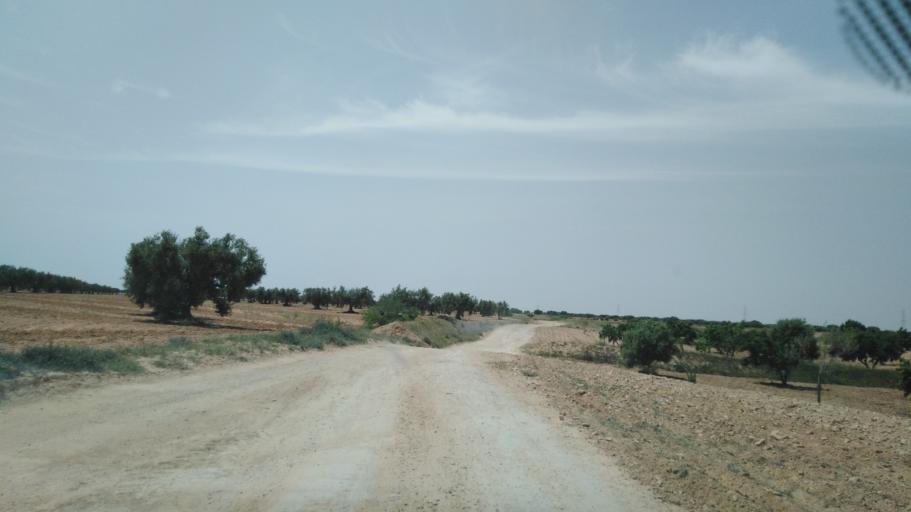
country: TN
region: Safaqis
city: Sfax
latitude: 34.7188
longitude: 10.5683
